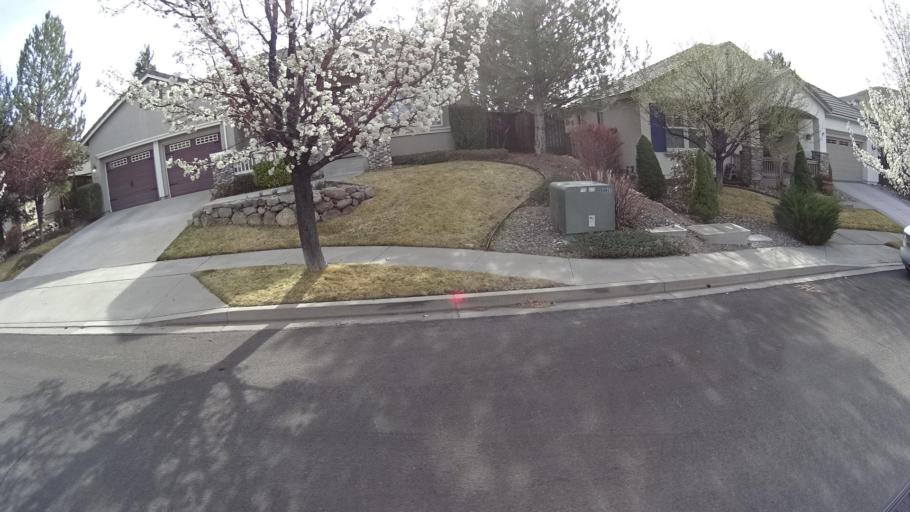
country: US
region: Nevada
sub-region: Washoe County
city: Mogul
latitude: 39.5320
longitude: -119.9159
